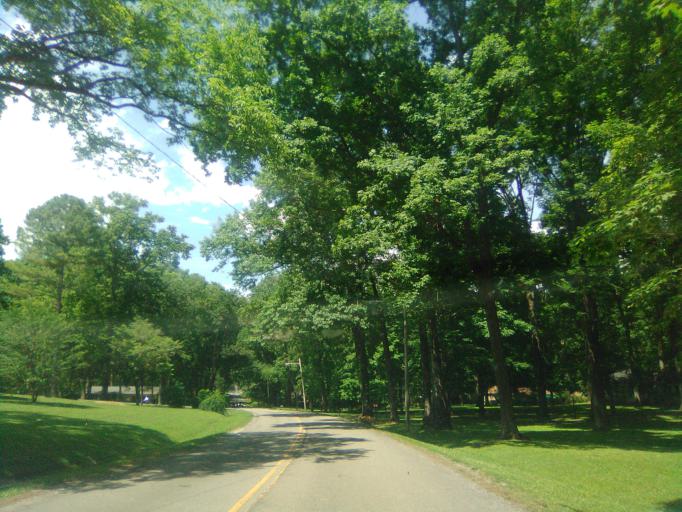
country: US
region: Tennessee
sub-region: Davidson County
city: Belle Meade
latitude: 36.1140
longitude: -86.8743
